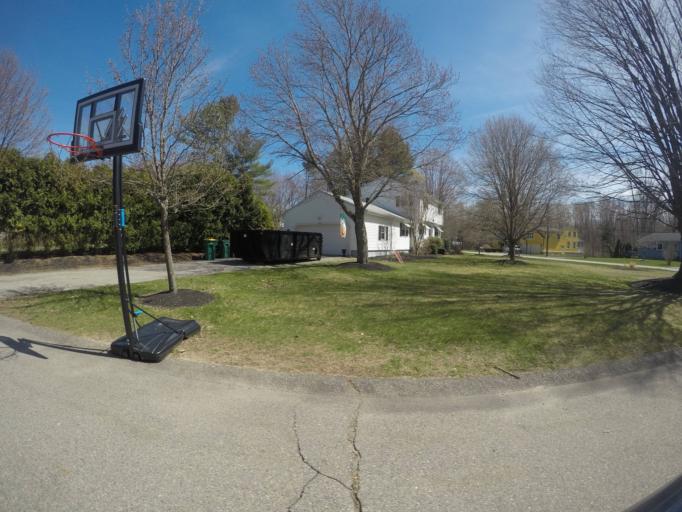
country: US
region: Massachusetts
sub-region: Bristol County
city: Easton
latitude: 42.0318
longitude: -71.1020
